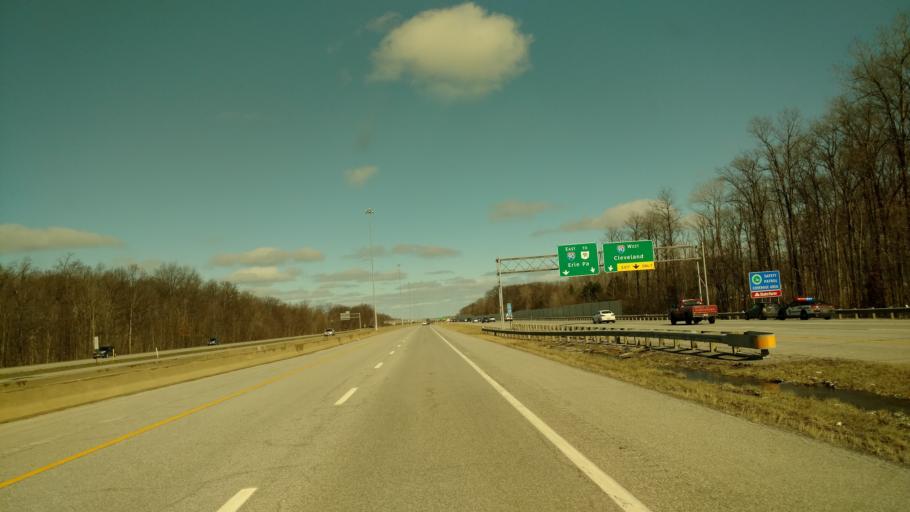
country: US
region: Ohio
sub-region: Cuyahoga County
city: Mayfield
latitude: 41.5748
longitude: -81.4473
